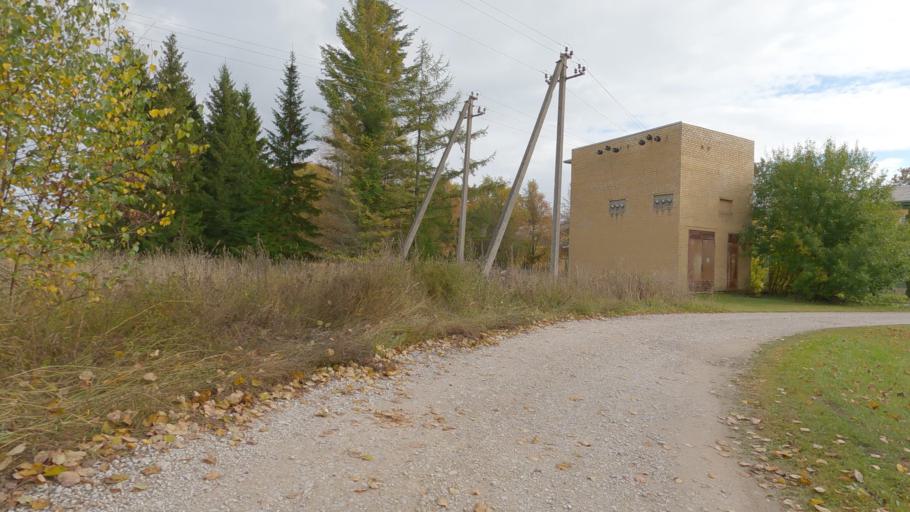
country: EE
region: Raplamaa
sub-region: Rapla vald
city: Rapla
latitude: 58.9360
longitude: 24.7523
